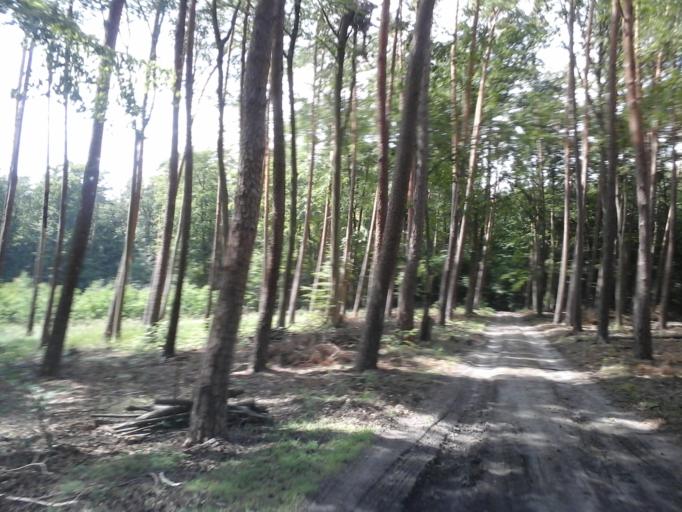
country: PL
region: West Pomeranian Voivodeship
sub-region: Powiat choszczenski
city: Bierzwnik
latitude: 53.0727
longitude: 15.6693
